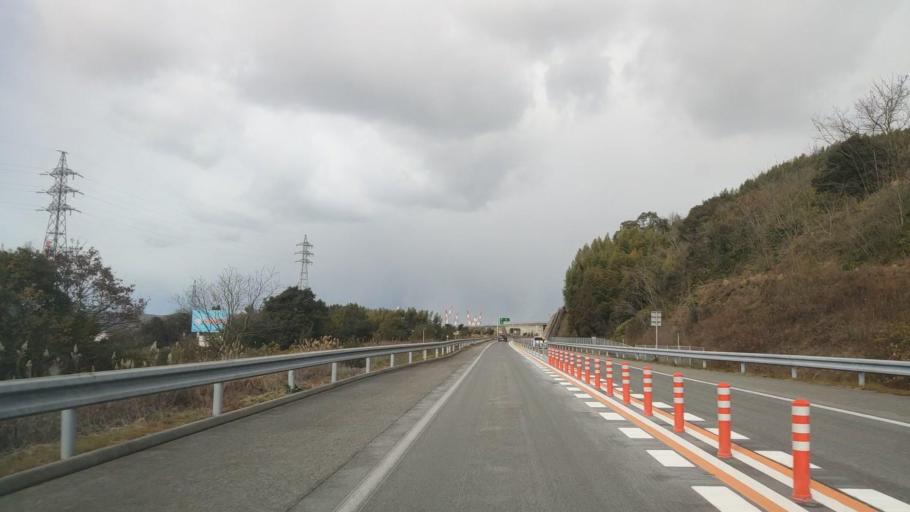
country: JP
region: Ehime
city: Hojo
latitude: 34.0929
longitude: 132.9784
